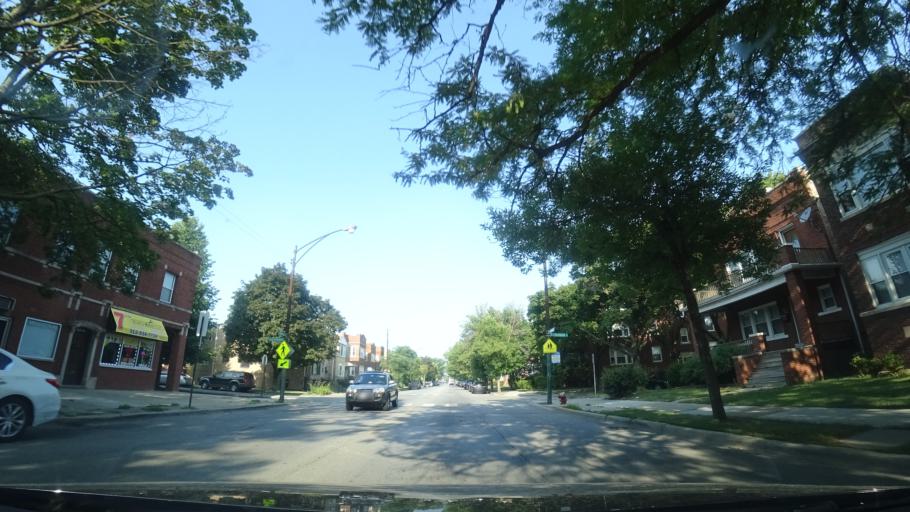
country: US
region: Illinois
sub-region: Cook County
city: Harwood Heights
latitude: 41.9606
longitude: -87.7594
